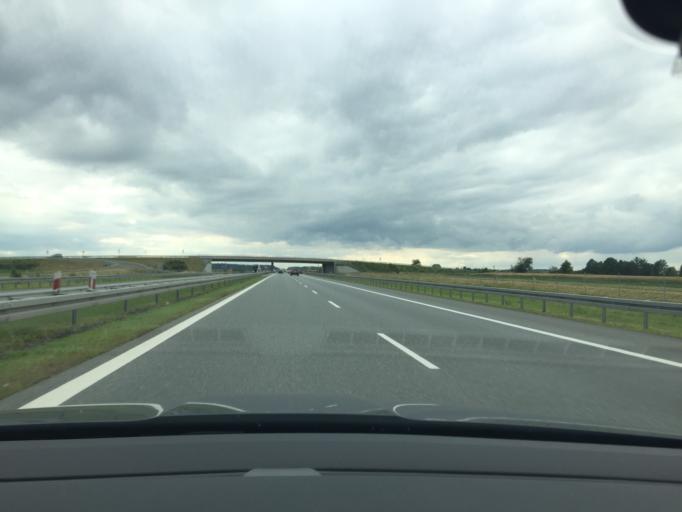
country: PL
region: Greater Poland Voivodeship
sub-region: Powiat nowotomyski
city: Kuslin
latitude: 52.3809
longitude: 16.3363
